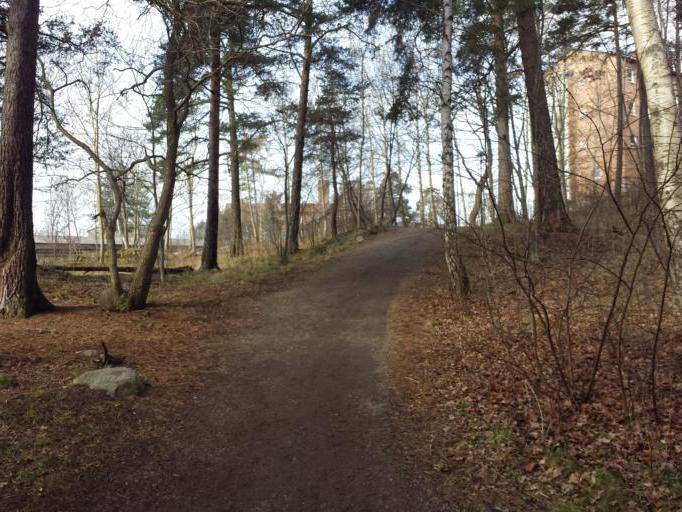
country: SE
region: Stockholm
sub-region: Nacka Kommun
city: Nacka
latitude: 59.2887
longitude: 18.1167
